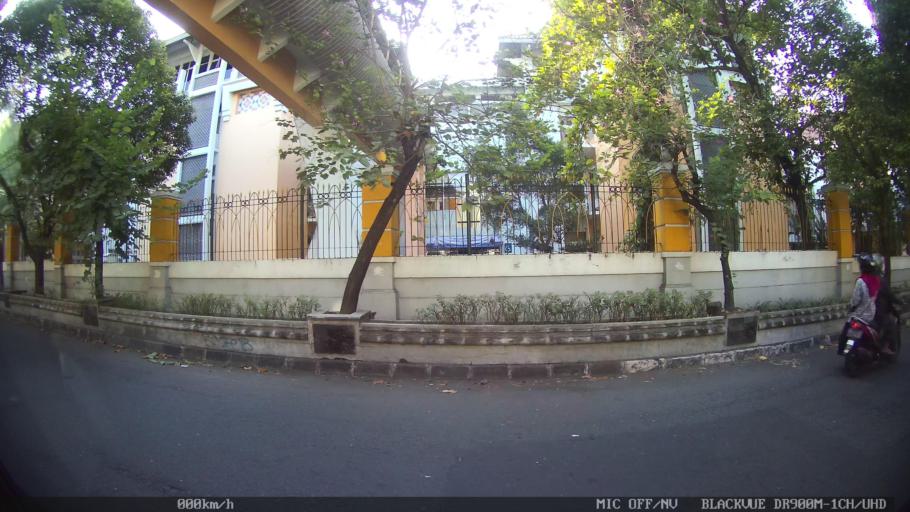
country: ID
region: Daerah Istimewa Yogyakarta
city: Yogyakarta
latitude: -7.7843
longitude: 110.3953
